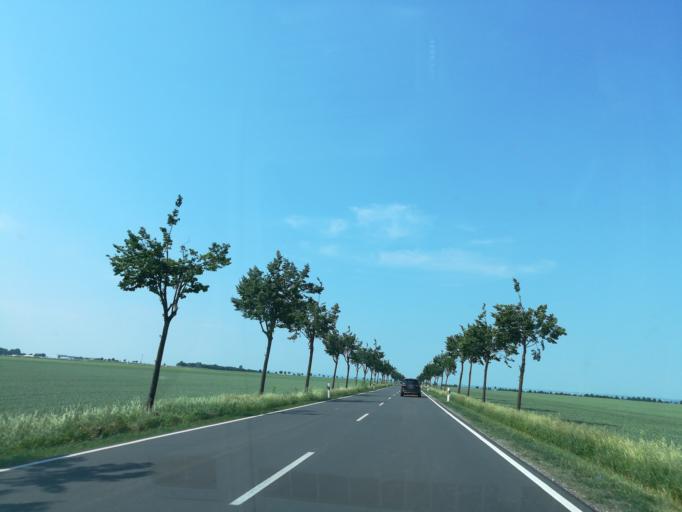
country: DE
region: Saxony-Anhalt
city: Gross Bornecke
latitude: 51.8503
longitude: 11.4531
